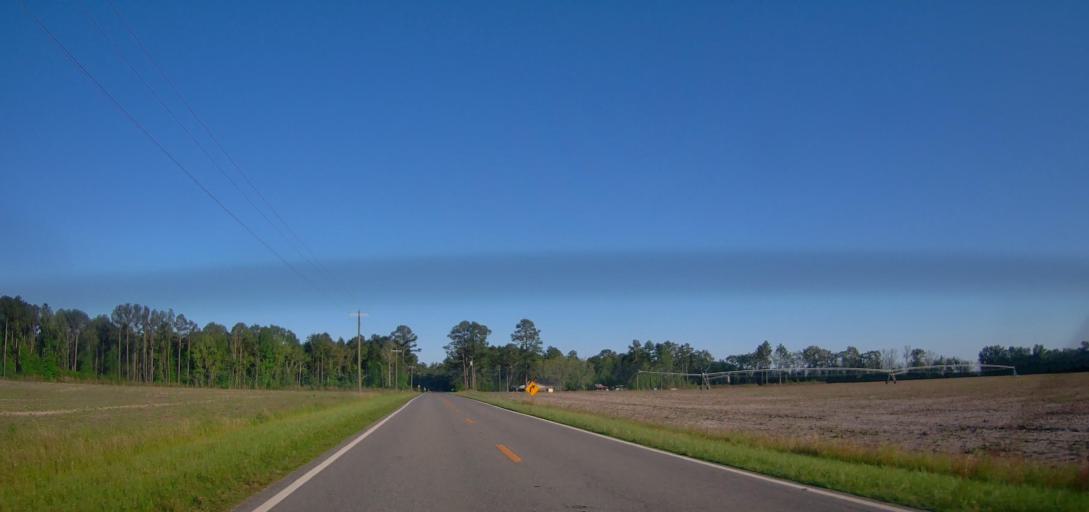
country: US
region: Georgia
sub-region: Ben Hill County
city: Fitzgerald
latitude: 31.6615
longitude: -83.1788
